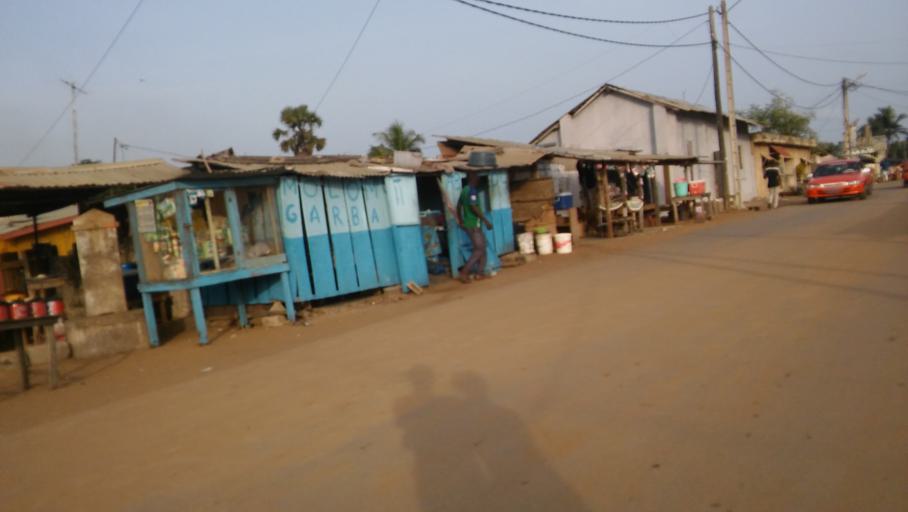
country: CI
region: Sud-Comoe
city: Grand-Bassam
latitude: 5.1949
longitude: -3.7274
